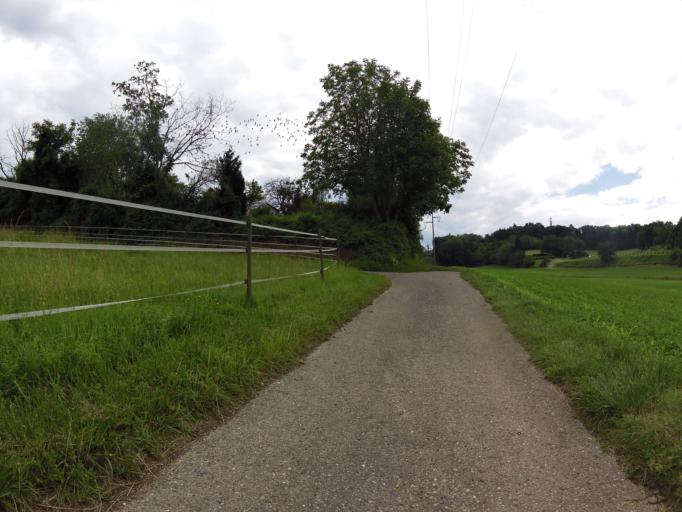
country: DE
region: Baden-Wuerttemberg
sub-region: Freiburg Region
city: Lahr
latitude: 48.3582
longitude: 7.8590
